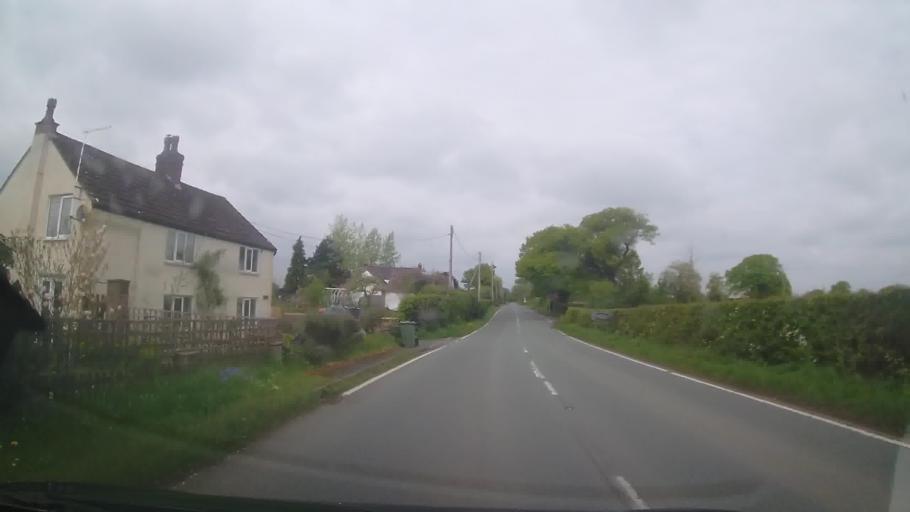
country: GB
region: Wales
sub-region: Wrexham
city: Overton
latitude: 52.9559
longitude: -2.8977
